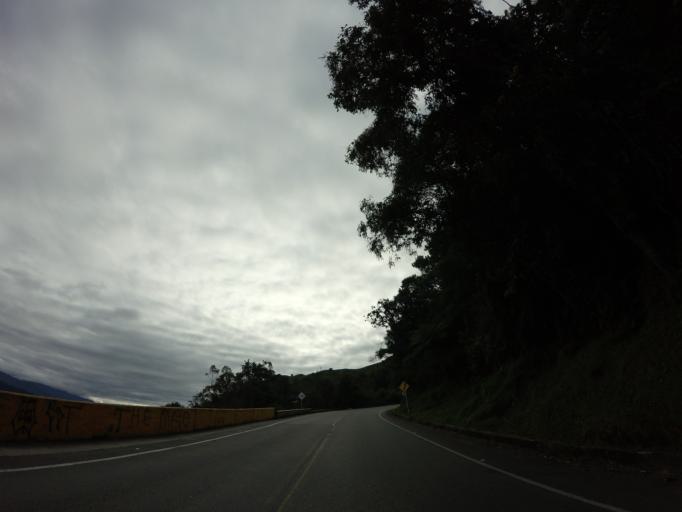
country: CO
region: Tolima
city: Herveo
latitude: 5.0995
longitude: -75.2327
